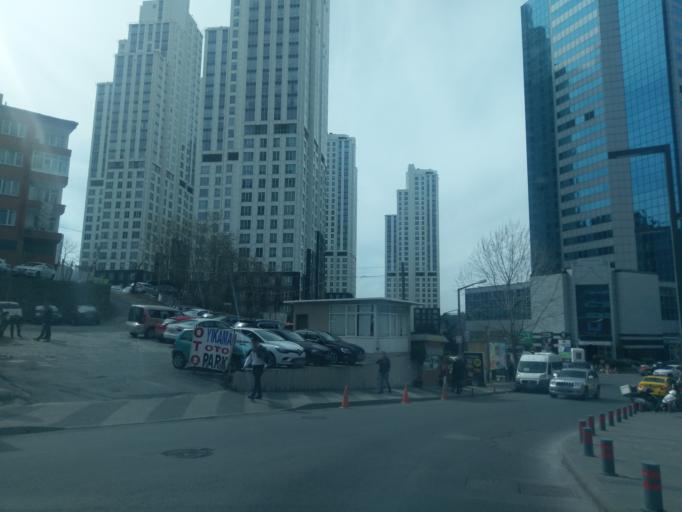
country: TR
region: Istanbul
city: Sisli
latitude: 41.1120
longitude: 29.0197
